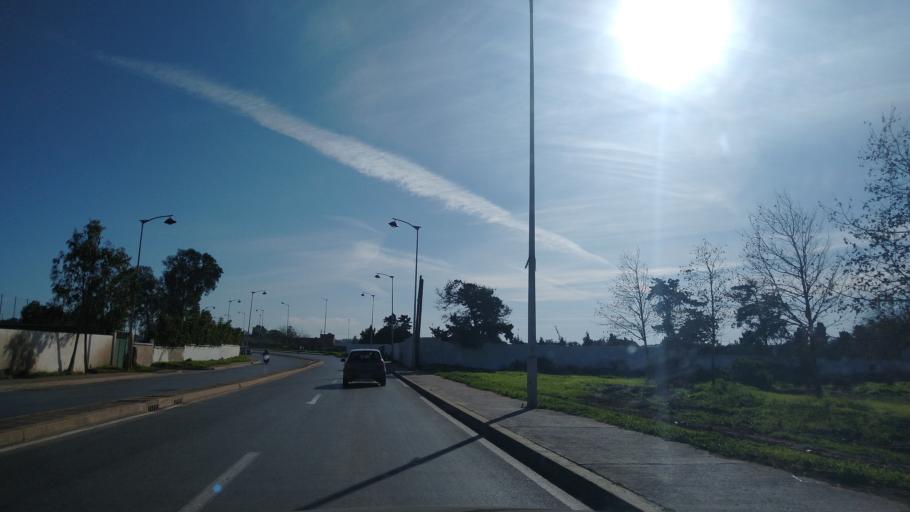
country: MA
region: Rabat-Sale-Zemmour-Zaer
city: Sale
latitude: 34.0254
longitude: -6.7353
